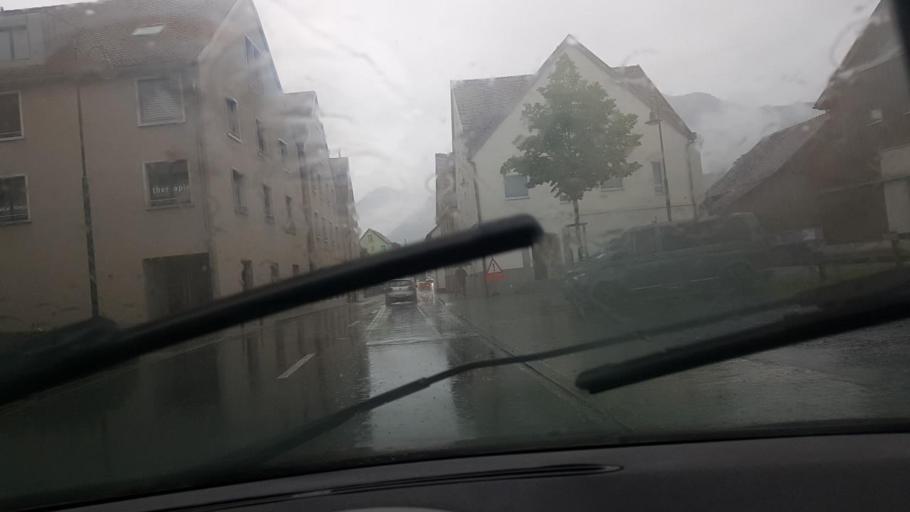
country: LI
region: Balzers
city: Balzers
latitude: 47.0683
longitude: 9.5072
